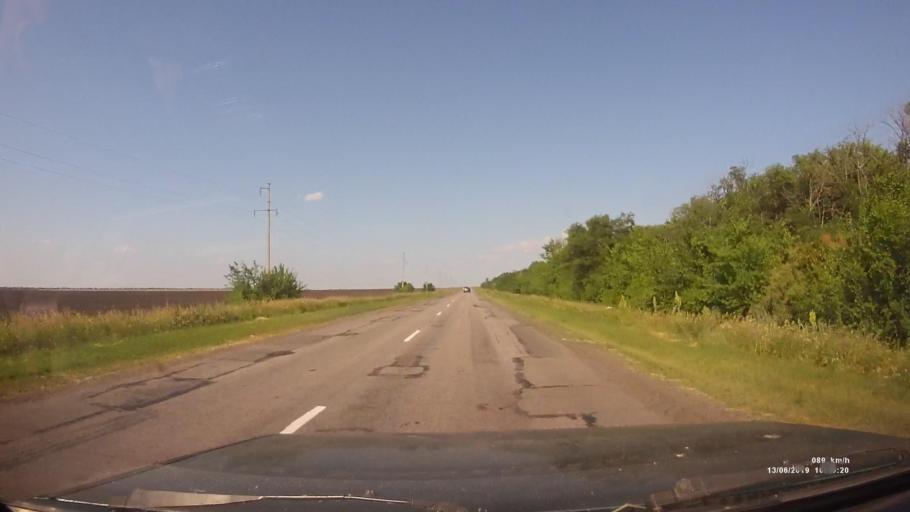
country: RU
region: Rostov
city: Kazanskaya
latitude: 49.8373
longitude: 41.2323
